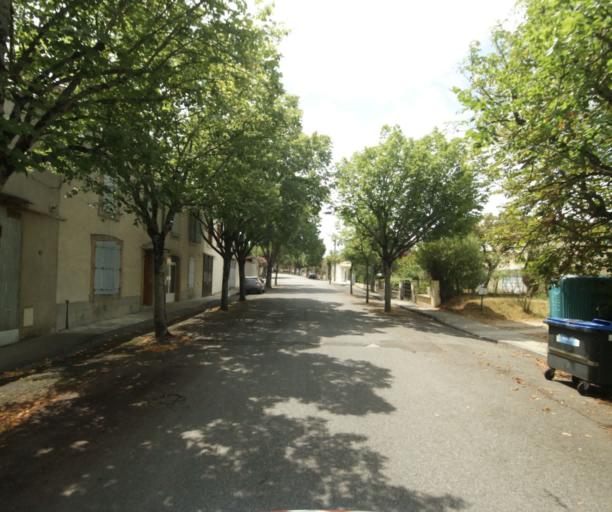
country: FR
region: Midi-Pyrenees
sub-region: Departement de la Haute-Garonne
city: Revel
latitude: 43.4553
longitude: 2.0017
